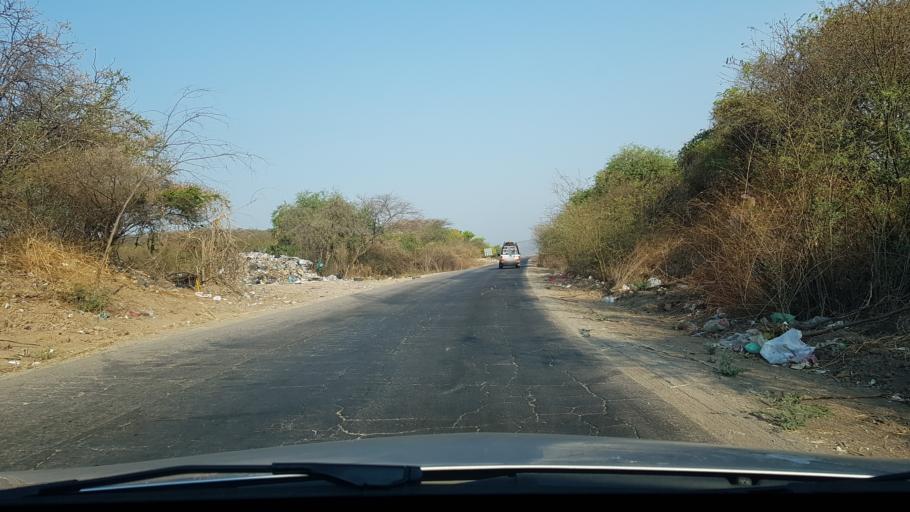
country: MX
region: Morelos
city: Tlaltizapan
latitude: 18.6760
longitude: -99.0766
